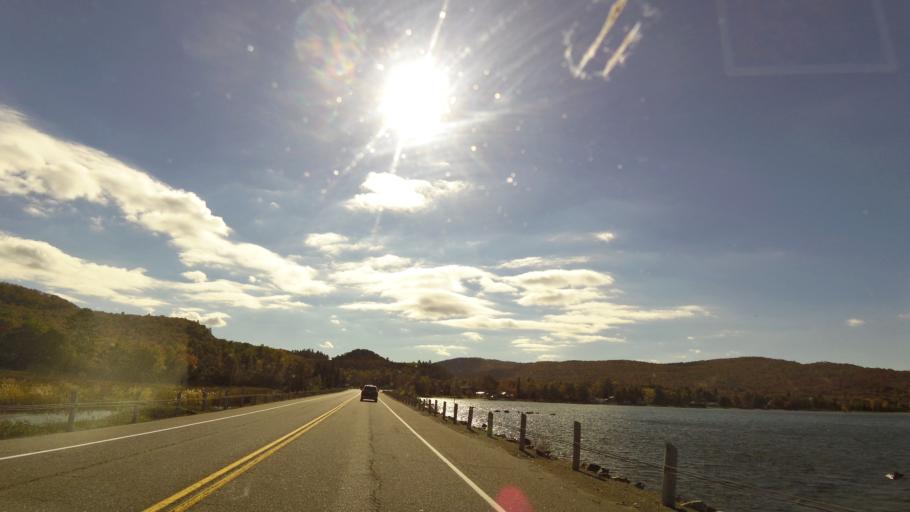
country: CA
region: Ontario
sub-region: Algoma
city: Sault Ste. Marie
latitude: 46.8216
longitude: -84.3995
